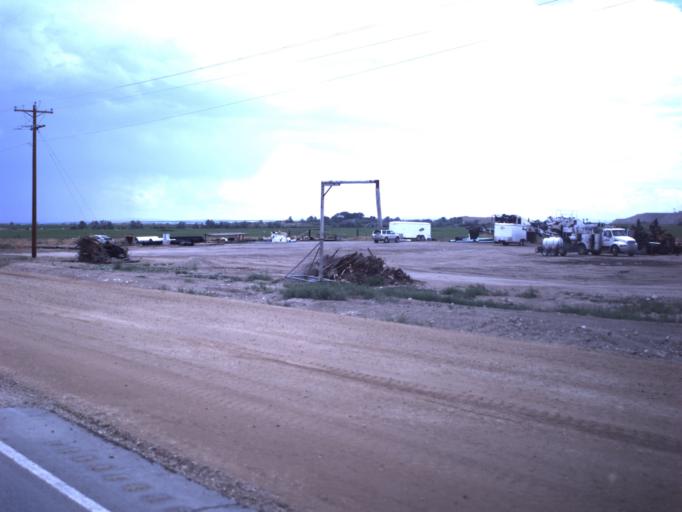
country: US
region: Utah
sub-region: Duchesne County
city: Roosevelt
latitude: 40.2400
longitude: -110.0675
